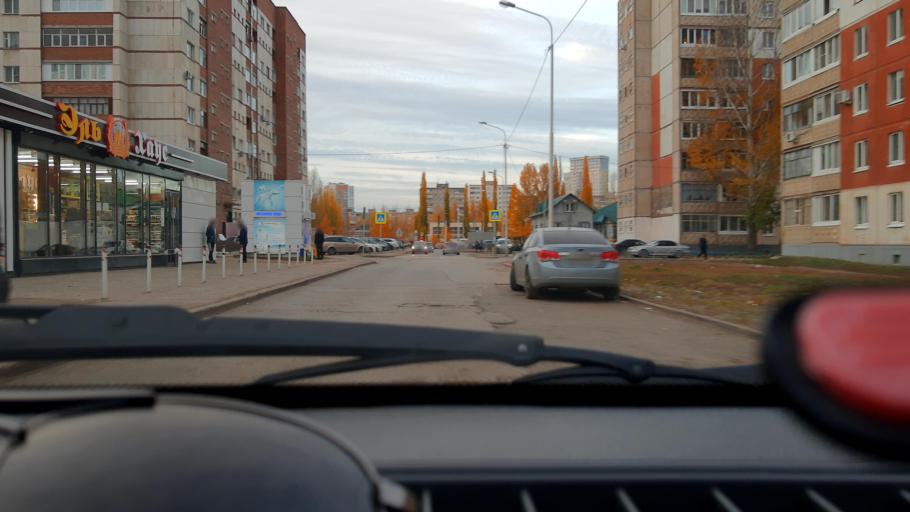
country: RU
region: Bashkortostan
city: Ufa
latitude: 54.7627
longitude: 56.0567
